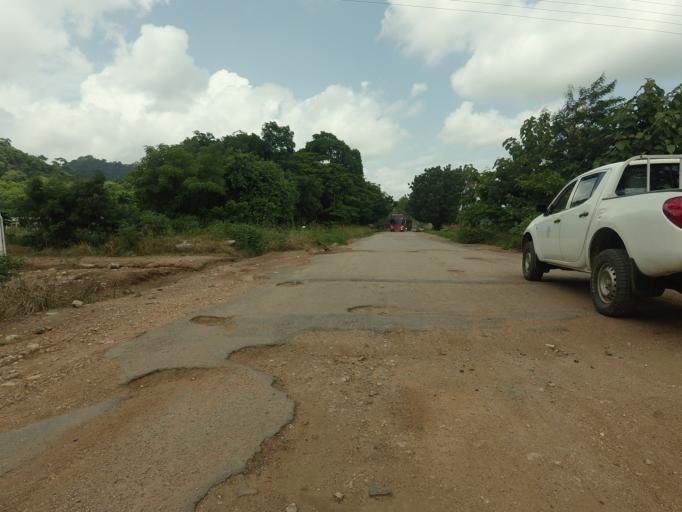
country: GH
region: Volta
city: Ho
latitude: 6.7282
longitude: 0.3454
